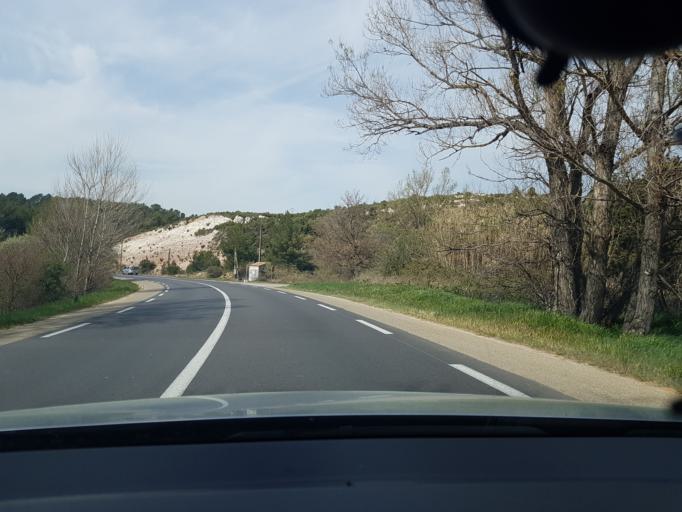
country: FR
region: Provence-Alpes-Cote d'Azur
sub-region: Departement des Bouches-du-Rhone
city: Gardanne
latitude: 43.4703
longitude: 5.4607
